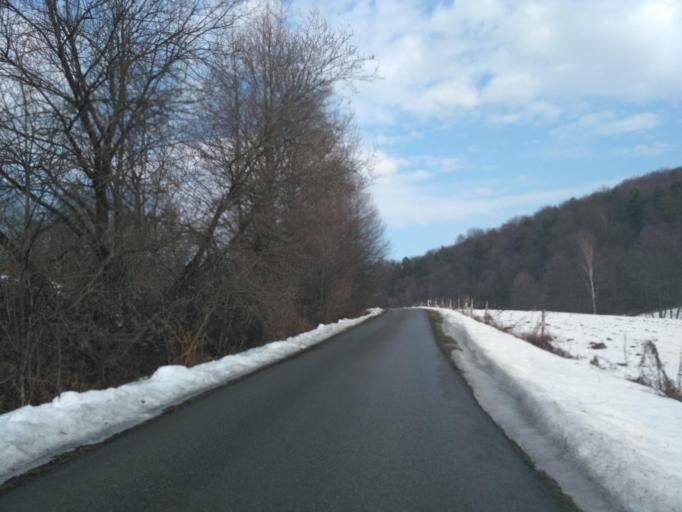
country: PL
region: Subcarpathian Voivodeship
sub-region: Powiat brzozowski
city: Niebocko
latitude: 49.6465
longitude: 22.1306
